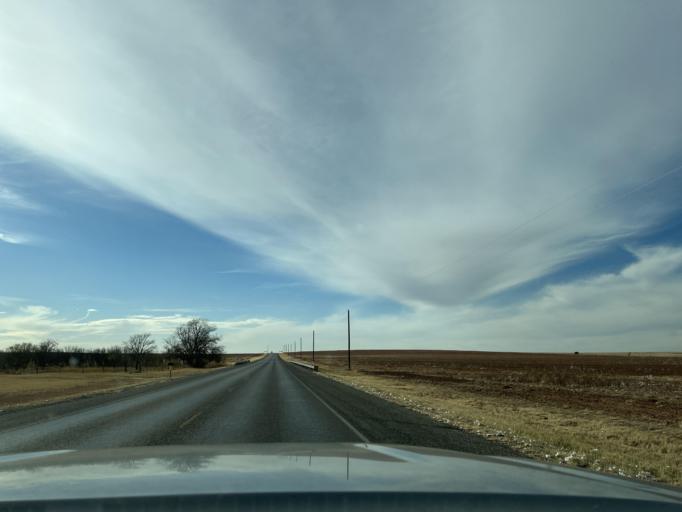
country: US
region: Texas
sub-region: Fisher County
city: Roby
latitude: 32.7408
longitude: -100.4824
